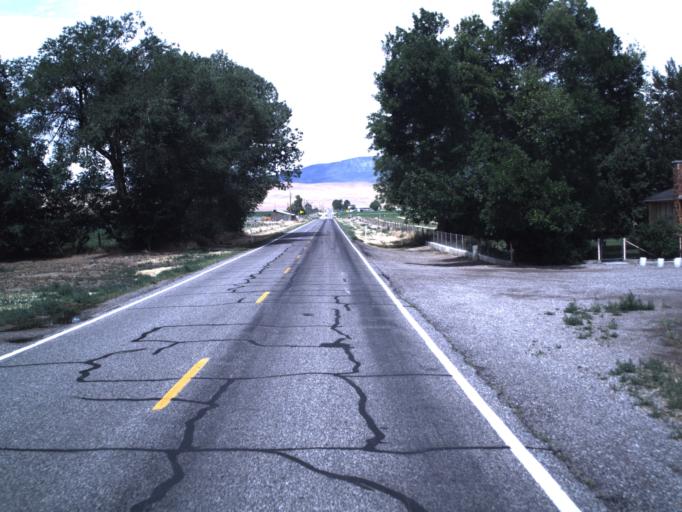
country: US
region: Utah
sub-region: Sevier County
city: Monroe
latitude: 38.6291
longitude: -112.1428
